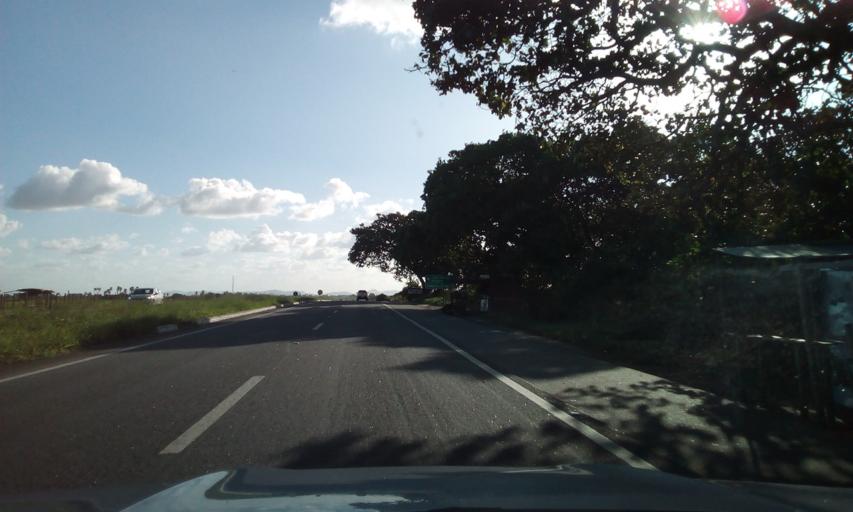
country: BR
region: Paraiba
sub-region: Pilar
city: Pilar
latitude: -7.1874
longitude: -35.2095
